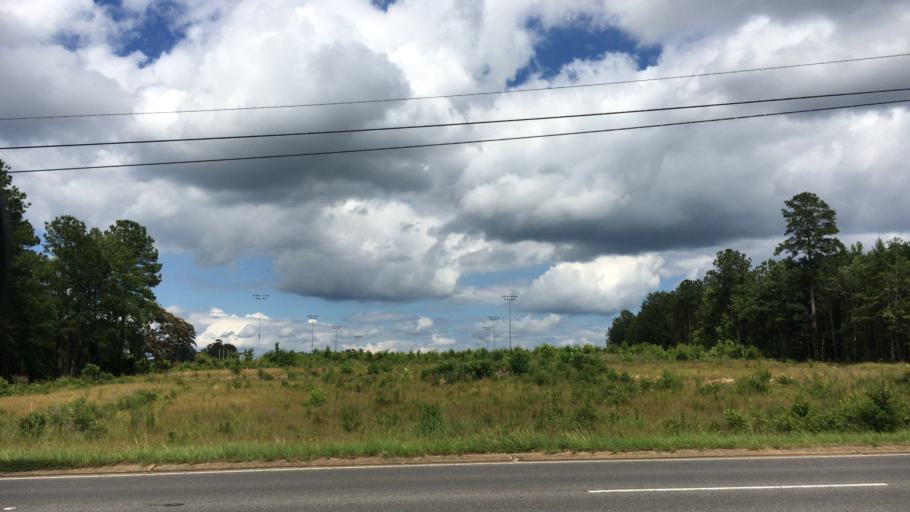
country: US
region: Louisiana
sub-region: Lincoln Parish
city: Ruston
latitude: 32.5026
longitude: -92.6370
